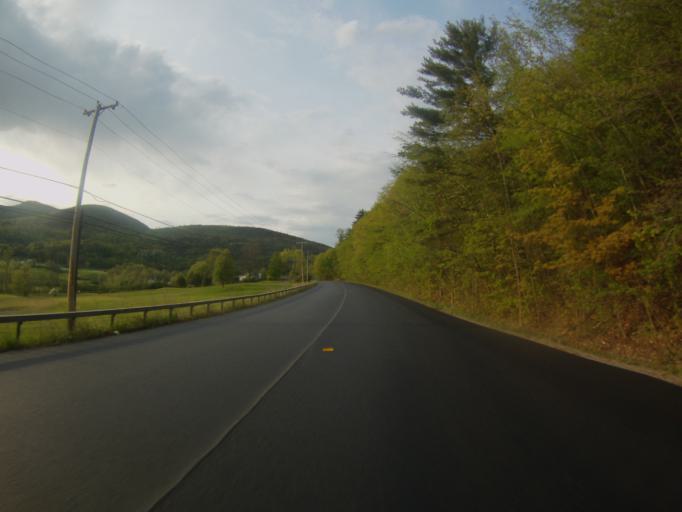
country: US
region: New York
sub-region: Essex County
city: Ticonderoga
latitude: 43.8360
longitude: -73.4609
